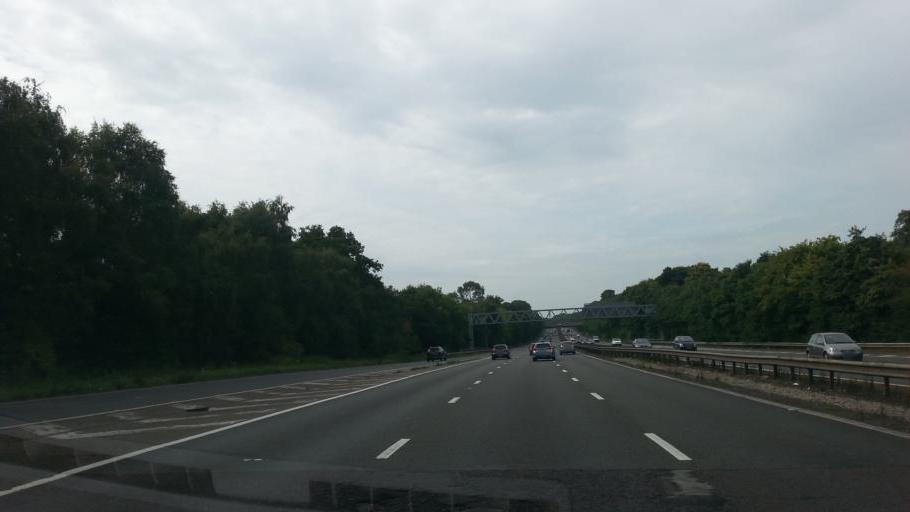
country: GB
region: England
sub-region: Hertfordshire
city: Welwyn
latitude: 51.8221
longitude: -0.2138
